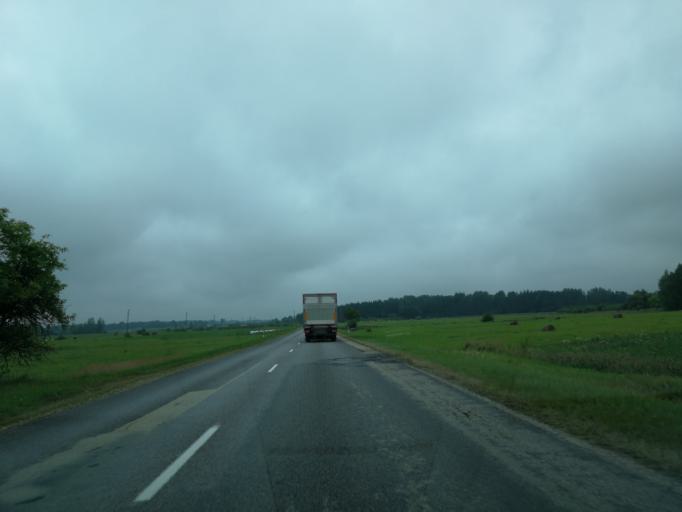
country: LV
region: Livani
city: Livani
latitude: 56.3478
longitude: 26.2763
